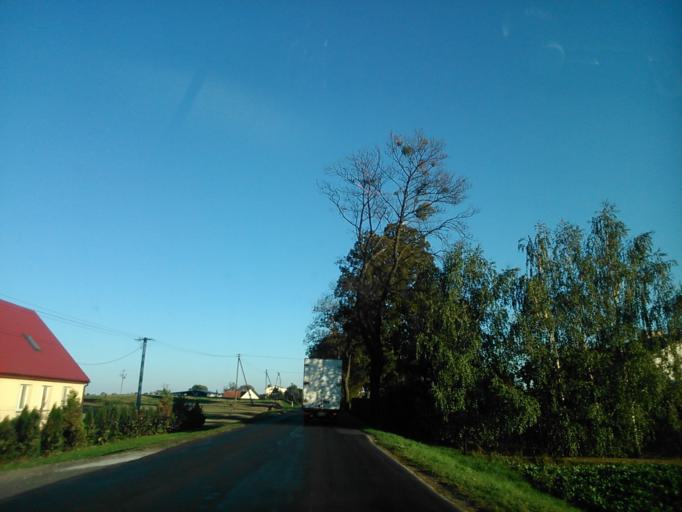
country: PL
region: Kujawsko-Pomorskie
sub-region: Powiat golubsko-dobrzynski
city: Golub-Dobrzyn
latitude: 53.1349
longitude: 19.0095
